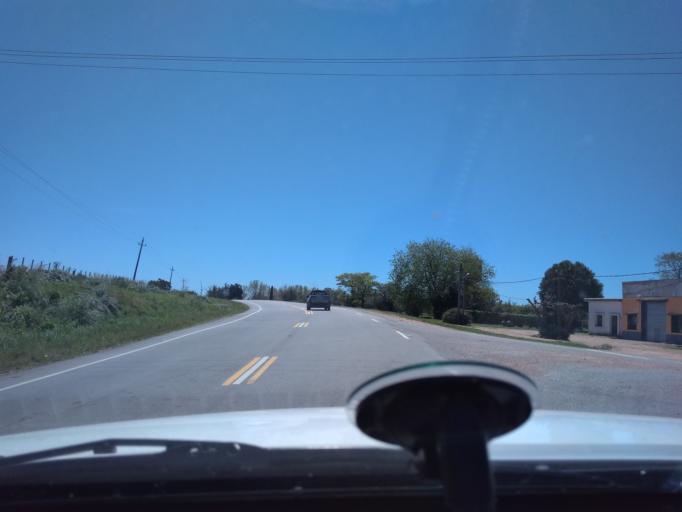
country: UY
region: Canelones
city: Las Piedras
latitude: -34.7108
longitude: -56.2907
